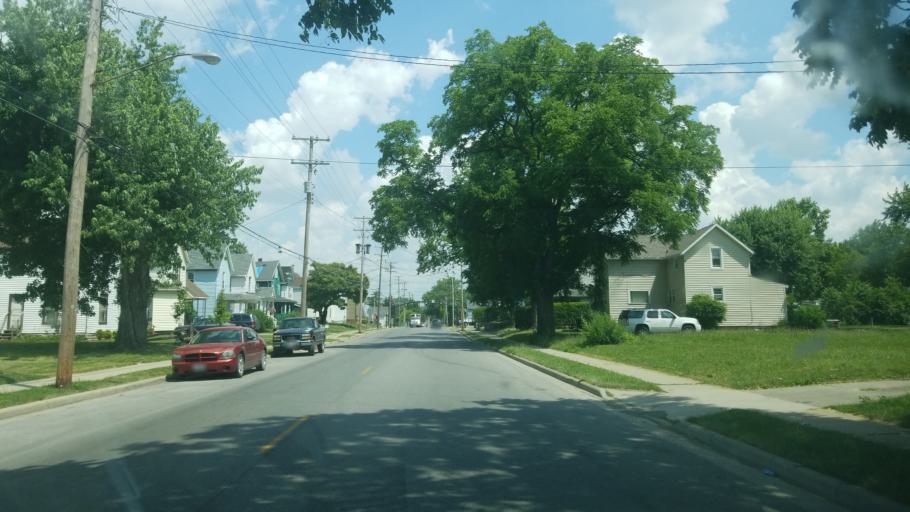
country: US
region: Ohio
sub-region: Allen County
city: Lima
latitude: 40.7288
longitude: -84.1134
